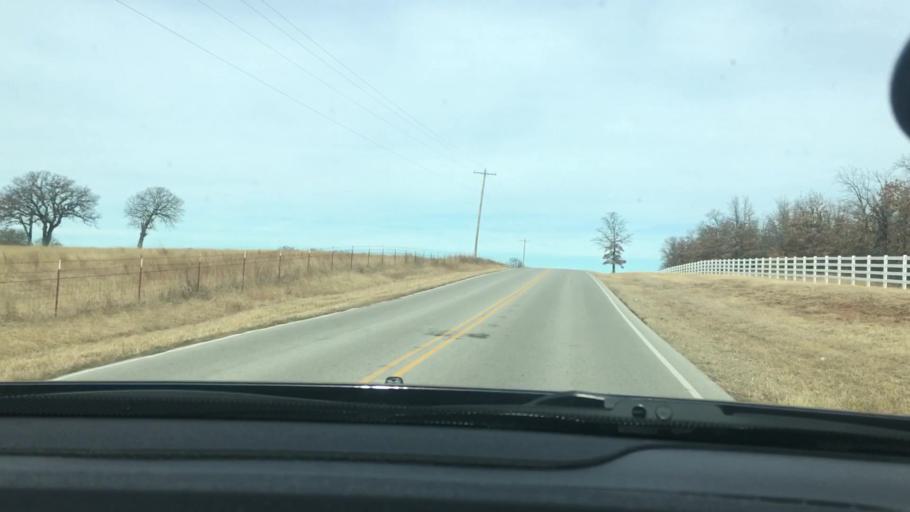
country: US
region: Oklahoma
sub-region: Carter County
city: Ardmore
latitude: 34.1821
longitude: -97.0731
